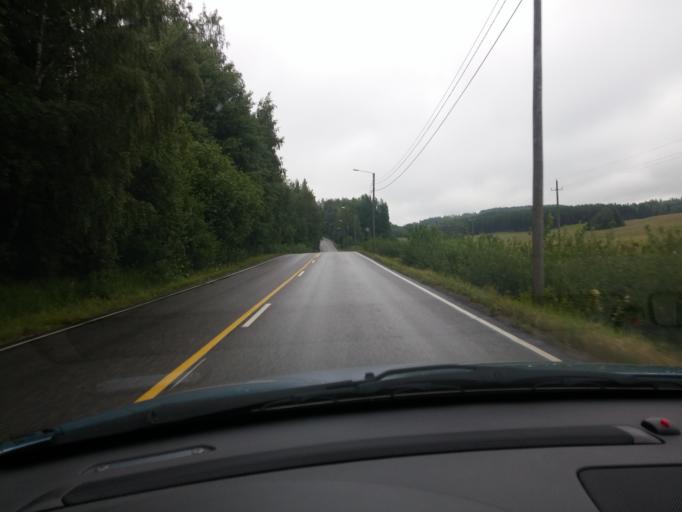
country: FI
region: Uusimaa
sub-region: Helsinki
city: Nurmijaervi
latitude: 60.3497
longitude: 24.7403
